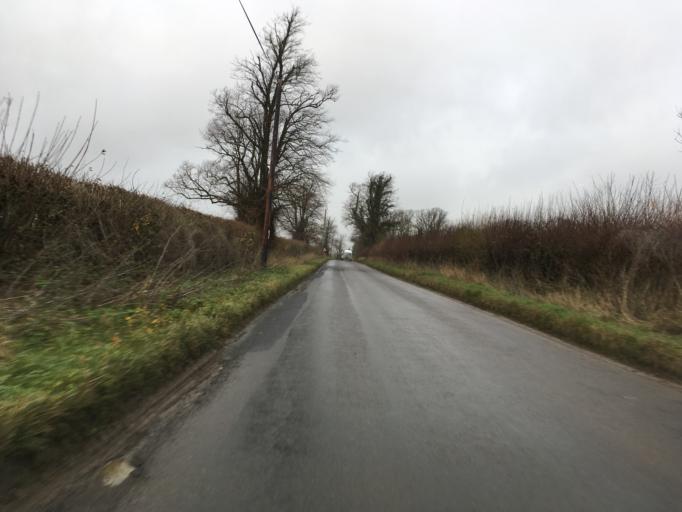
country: GB
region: England
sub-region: Wiltshire
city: Luckington
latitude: 51.5216
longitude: -2.2073
